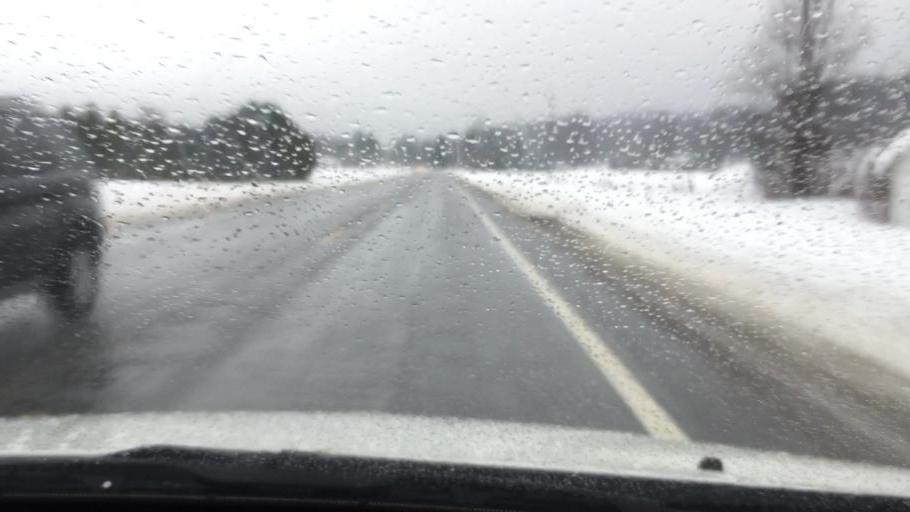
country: US
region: Michigan
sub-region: Charlevoix County
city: East Jordan
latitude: 45.0709
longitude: -85.0855
